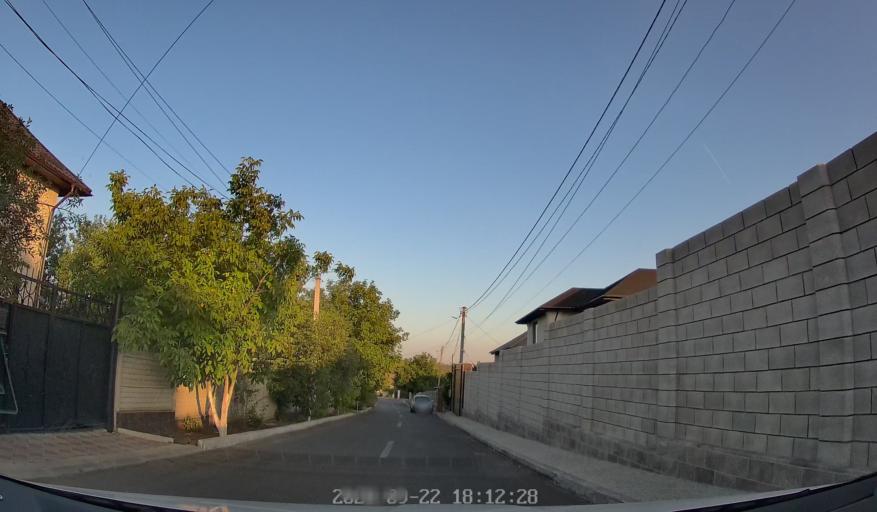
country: MD
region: Laloveni
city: Ialoveni
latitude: 46.9476
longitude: 28.7890
